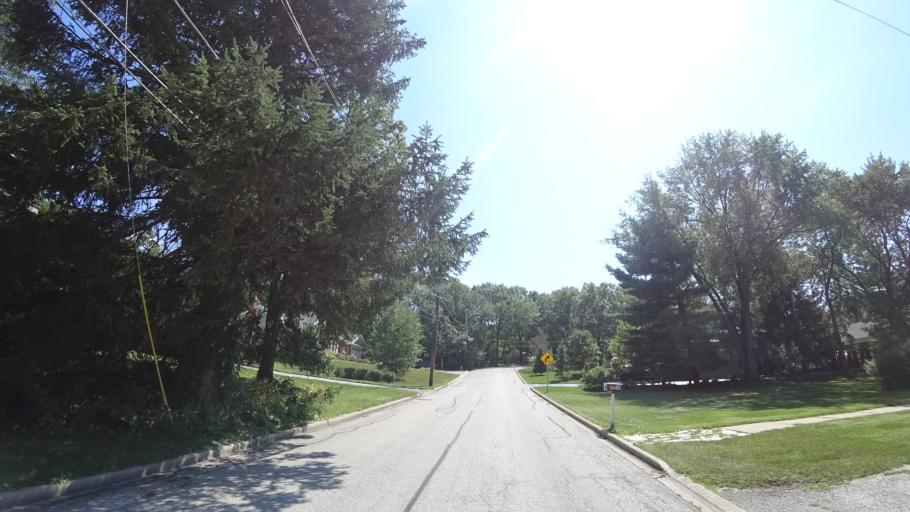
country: US
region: Illinois
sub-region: Cook County
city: Orland Park
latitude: 41.6265
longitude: -87.8591
